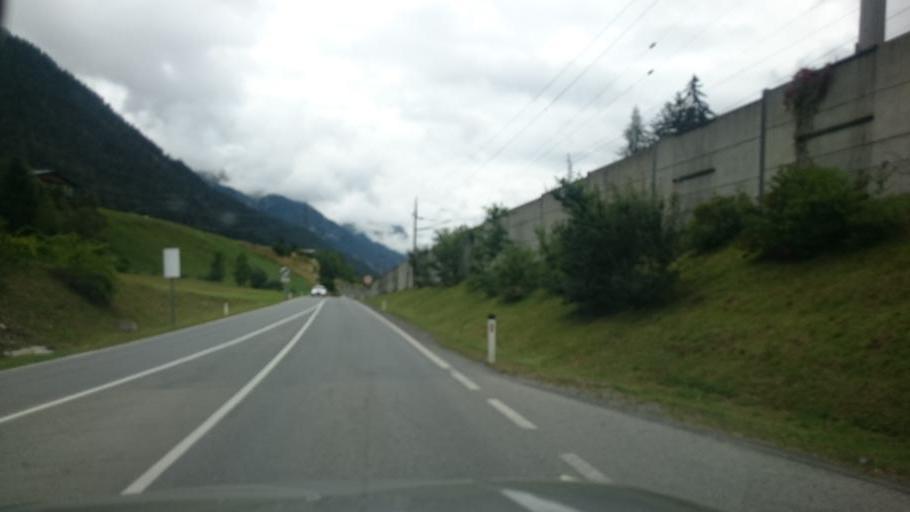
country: AT
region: Tyrol
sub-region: Politischer Bezirk Landeck
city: Sankt Anton am Arlberg
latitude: 47.1407
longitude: 10.2927
